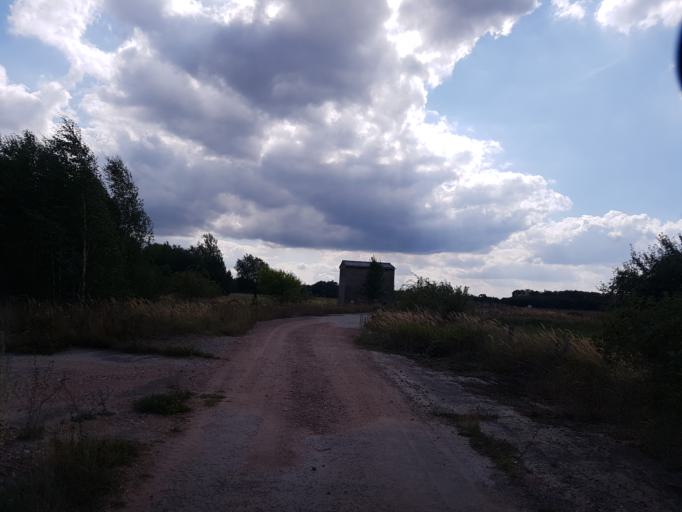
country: DE
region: Brandenburg
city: Finsterwalde
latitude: 51.6107
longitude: 13.7564
